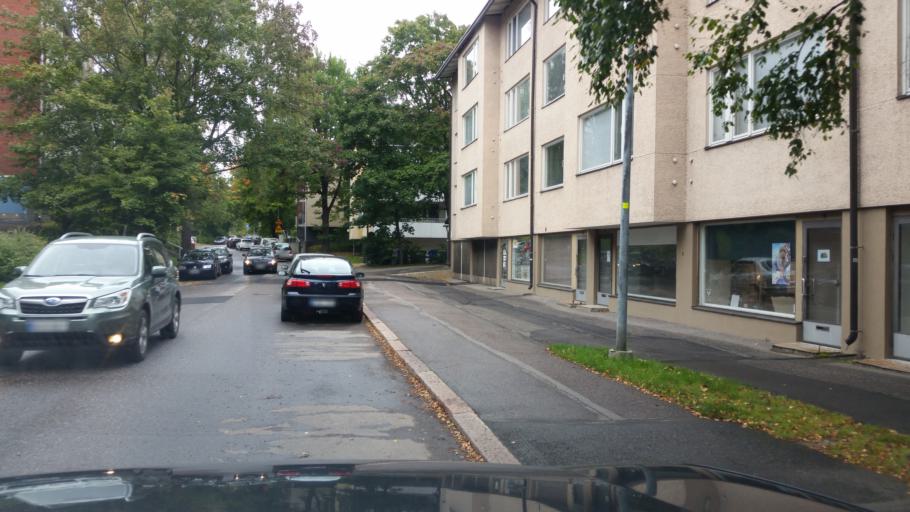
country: FI
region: Uusimaa
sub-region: Helsinki
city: Helsinki
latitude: 60.2149
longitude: 24.8954
